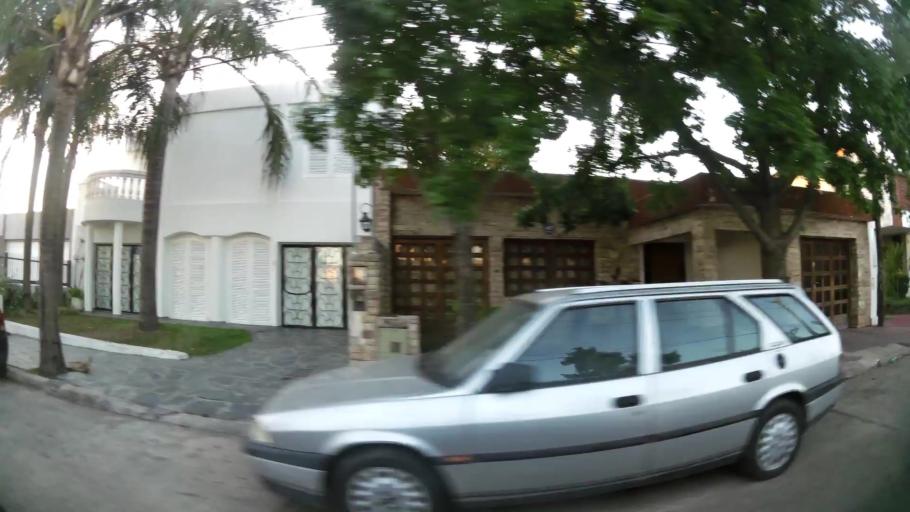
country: AR
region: Cordoba
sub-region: Departamento de Capital
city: Cordoba
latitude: -31.3802
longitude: -64.2208
